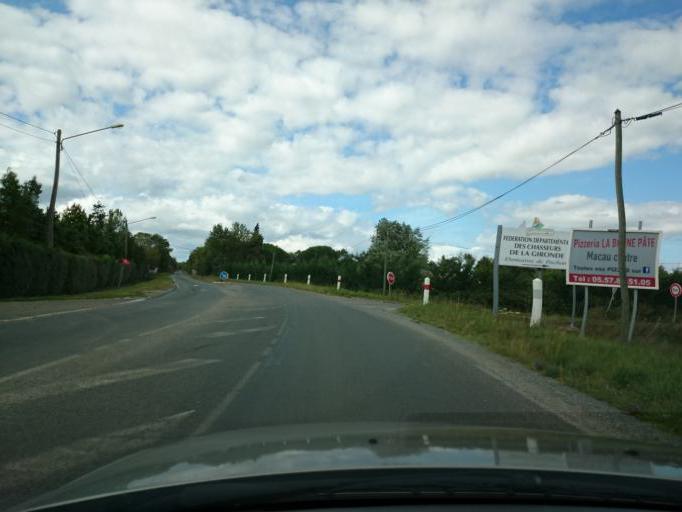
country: FR
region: Aquitaine
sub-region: Departement de la Gironde
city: Ludon-Medoc
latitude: 44.9813
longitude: -0.5644
